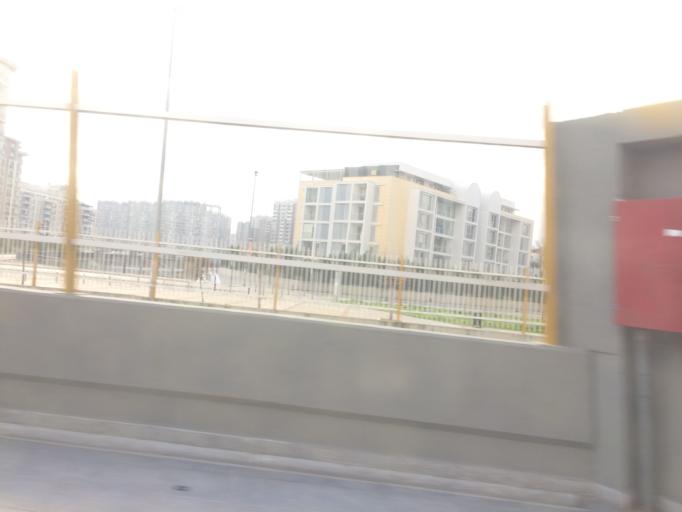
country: TR
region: Izmir
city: Karsiyaka
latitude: 38.4816
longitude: 27.0834
